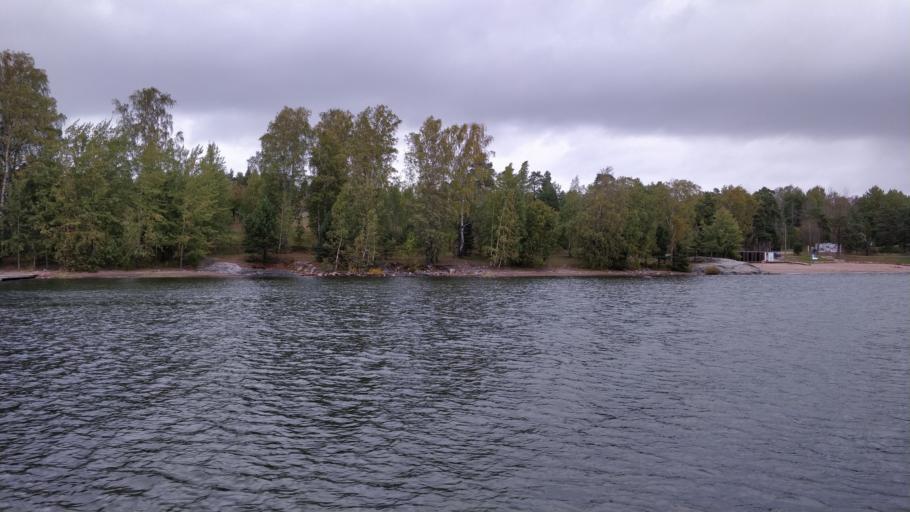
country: FI
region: Uusimaa
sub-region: Helsinki
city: Helsinki
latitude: 60.1775
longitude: 24.9914
